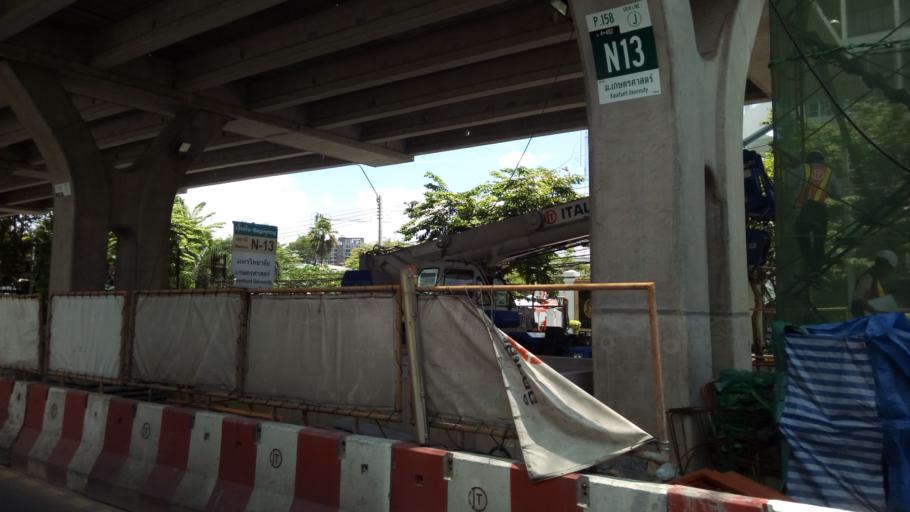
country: TH
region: Bangkok
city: Chatuchak
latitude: 13.8429
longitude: 100.5775
